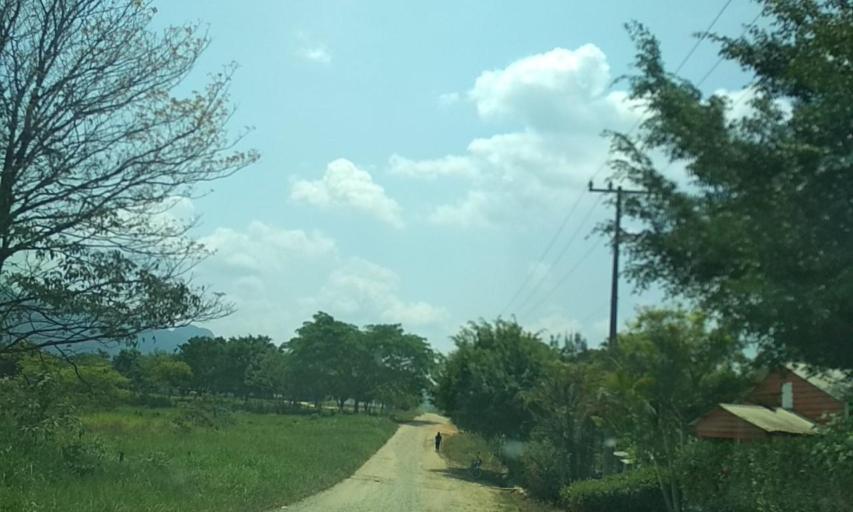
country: MX
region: Chiapas
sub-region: Tecpatan
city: Raudales Malpaso
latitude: 17.3445
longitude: -93.9631
